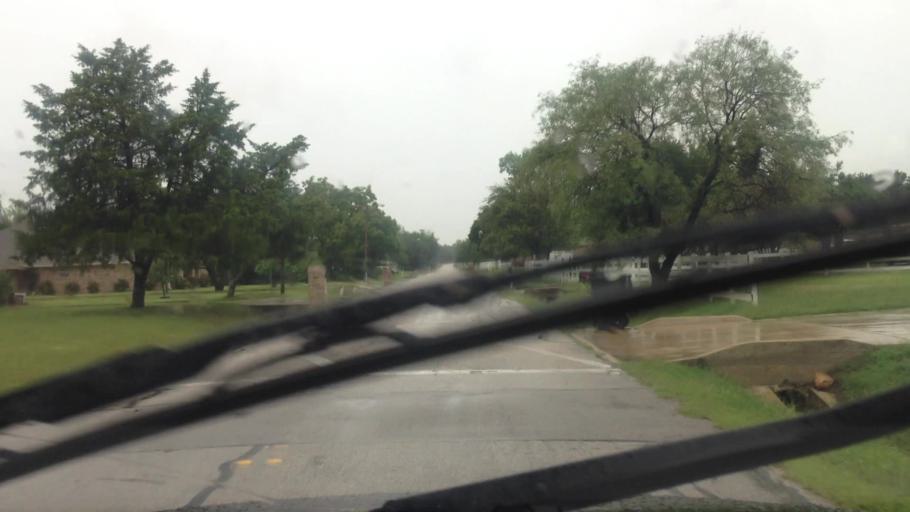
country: US
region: Texas
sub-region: Tarrant County
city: Watauga
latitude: 32.8695
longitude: -97.2254
